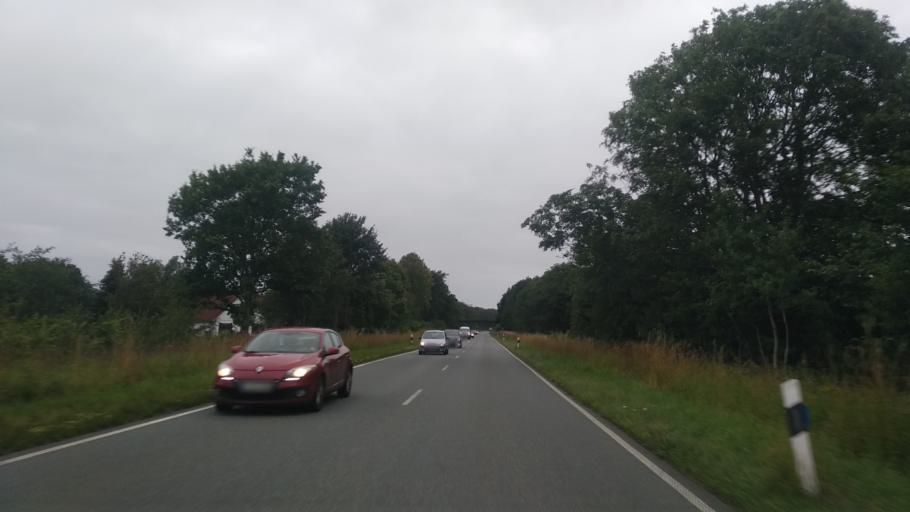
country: DE
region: Schleswig-Holstein
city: Sieverstedt
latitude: 54.6149
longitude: 9.4723
